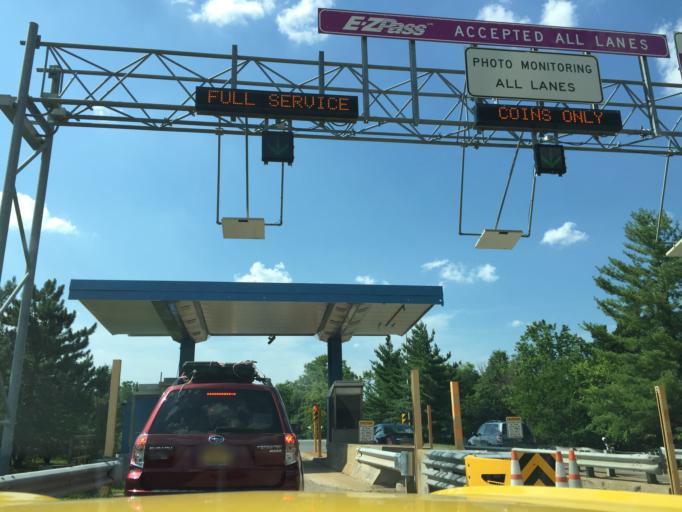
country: US
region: Virginia
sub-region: Loudoun County
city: Oak Grove
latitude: 38.9639
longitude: -77.4248
